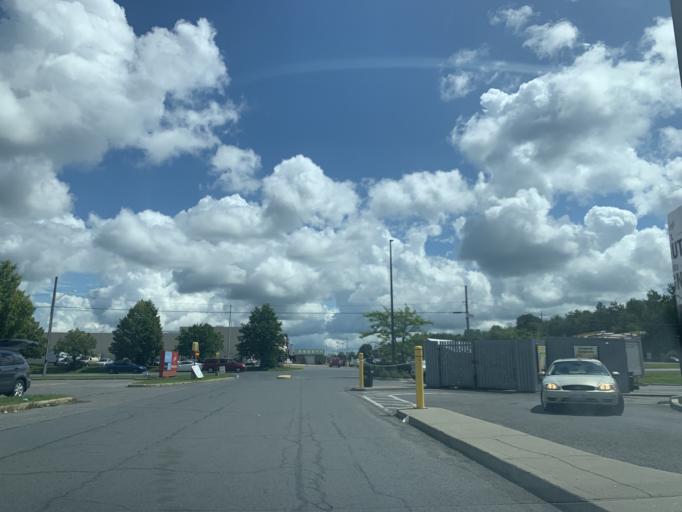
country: CA
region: Ontario
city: Hawkesbury
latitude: 45.5928
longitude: -74.6012
